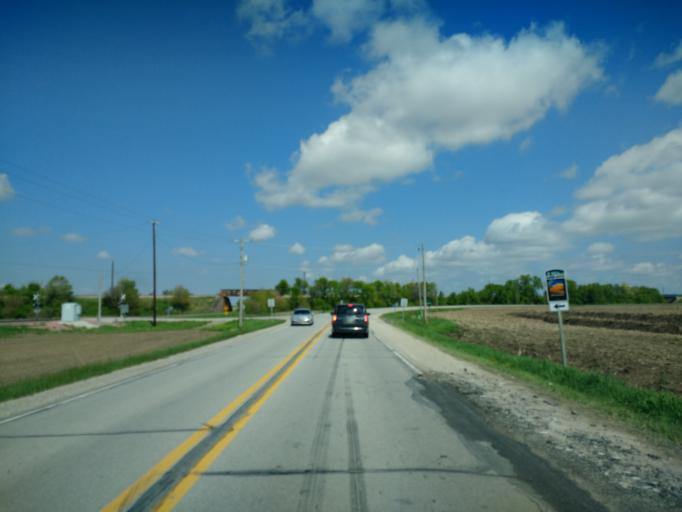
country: US
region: Iowa
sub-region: Harrison County
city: Missouri Valley
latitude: 41.4986
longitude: -95.8933
